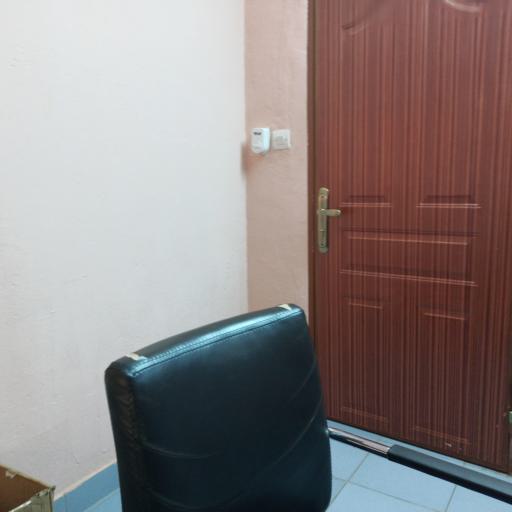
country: BF
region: Centre
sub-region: Kadiogo Province
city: Ouagadougou
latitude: 12.3857
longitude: -1.5268
